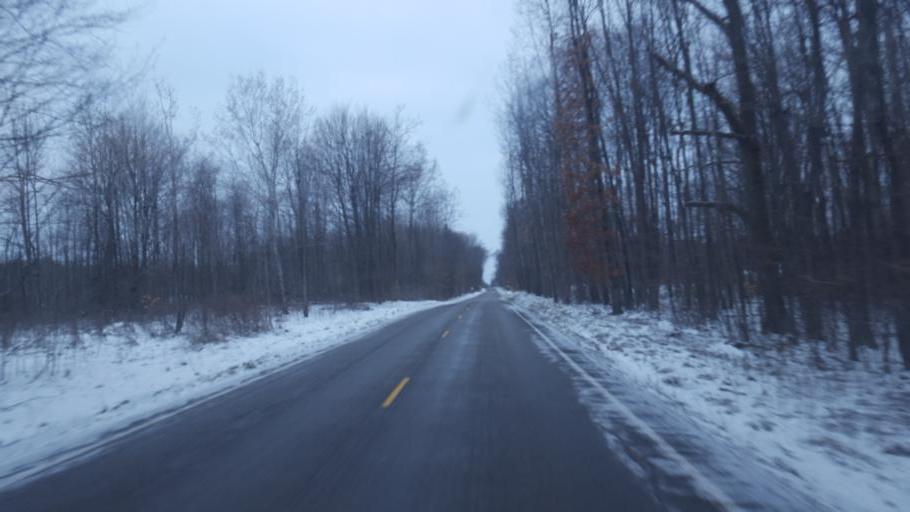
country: US
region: Pennsylvania
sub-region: Mercer County
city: Stoneboro
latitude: 41.4078
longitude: -80.0495
